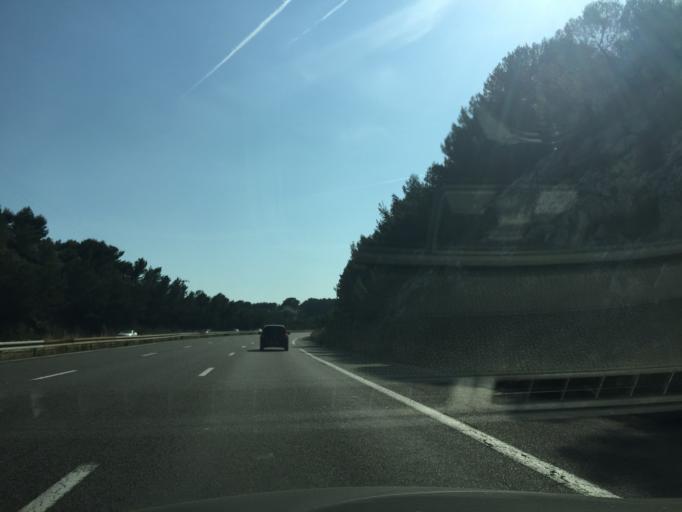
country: FR
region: Provence-Alpes-Cote d'Azur
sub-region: Departement des Bouches-du-Rhone
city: Martigues
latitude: 43.3952
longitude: 5.0671
